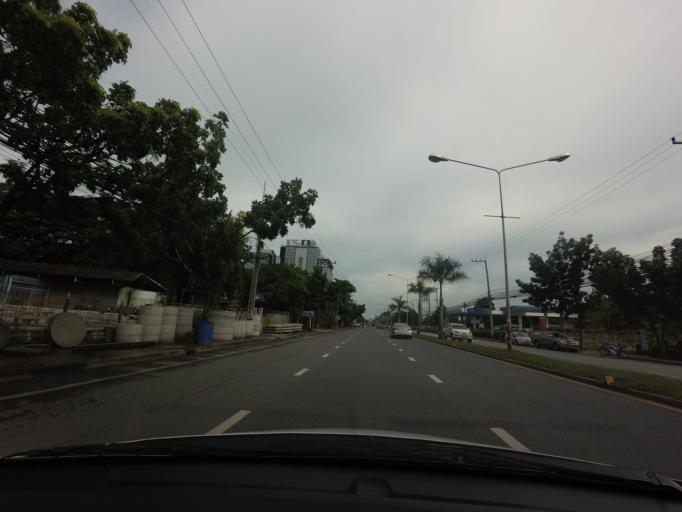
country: TH
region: Chachoengsao
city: Chachoengsao
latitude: 13.6696
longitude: 101.0871
